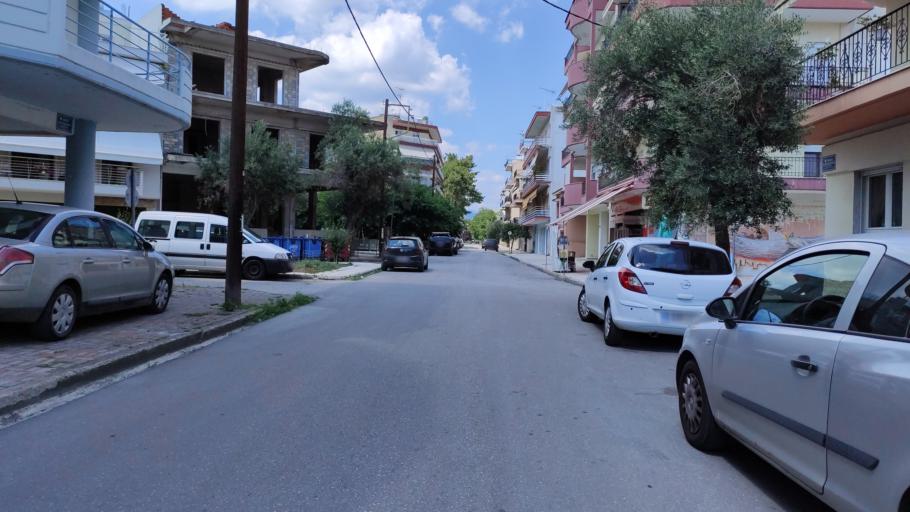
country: GR
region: East Macedonia and Thrace
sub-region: Nomos Rodopis
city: Komotini
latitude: 41.1124
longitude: 25.3949
